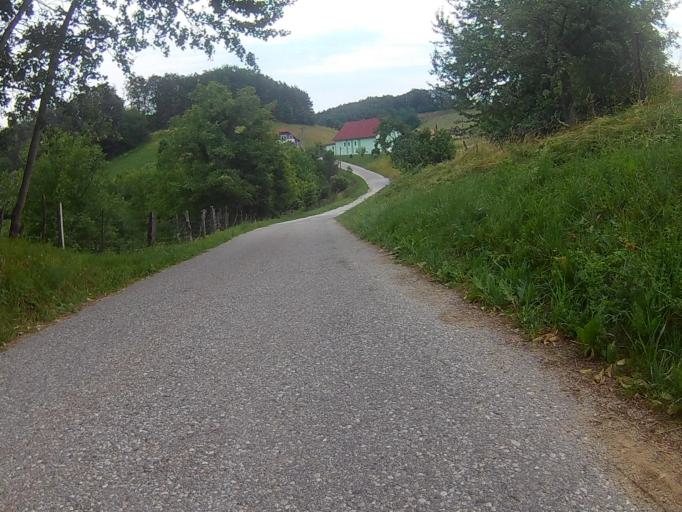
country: SI
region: Sentilj
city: Sentilj v Slov. Goricah
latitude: 46.6735
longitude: 15.6345
